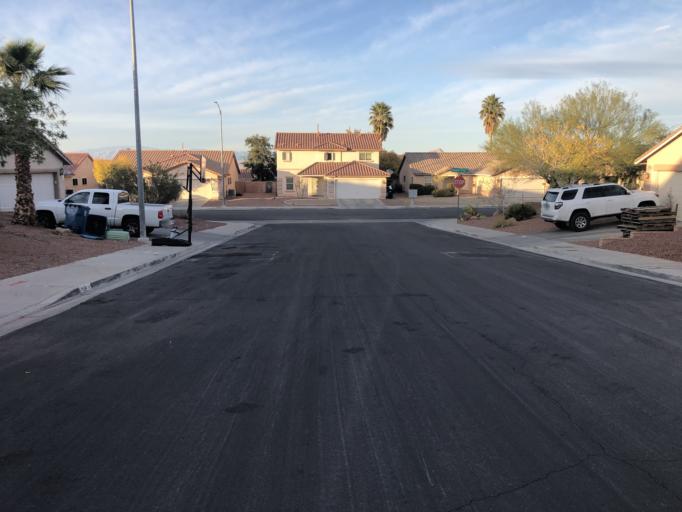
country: US
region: Nevada
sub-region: Clark County
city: Whitney
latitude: 36.0161
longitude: -115.0450
